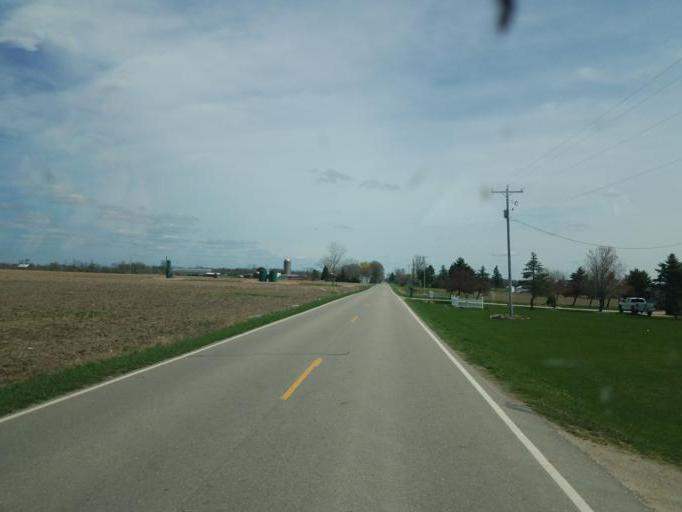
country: US
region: Michigan
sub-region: Isabella County
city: Mount Pleasant
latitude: 43.6698
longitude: -84.7192
